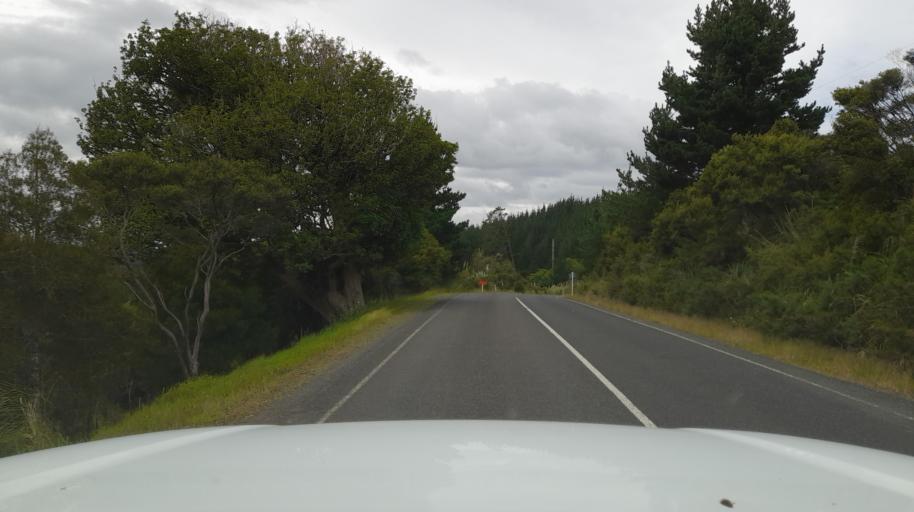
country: NZ
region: Northland
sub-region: Far North District
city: Kaitaia
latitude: -35.3676
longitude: 173.4114
